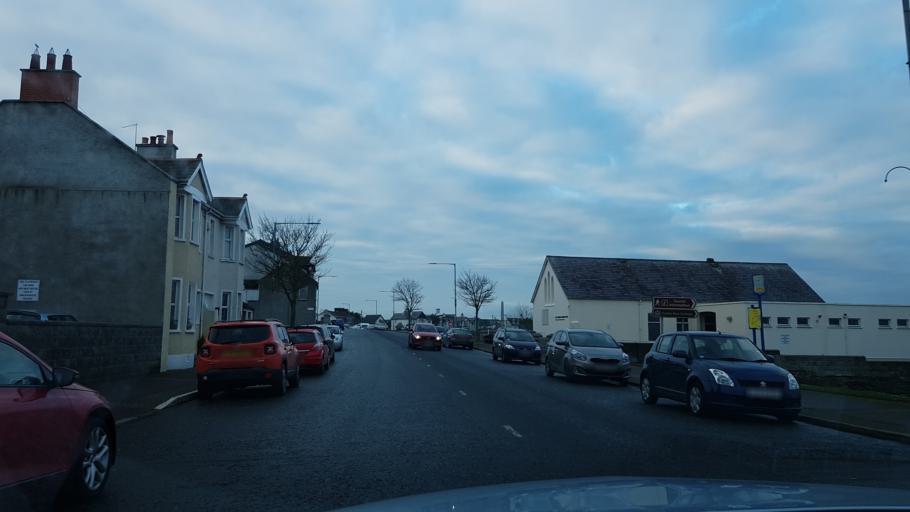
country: GB
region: Northern Ireland
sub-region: North Down District
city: Bangor
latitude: 54.6757
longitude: -5.6178
